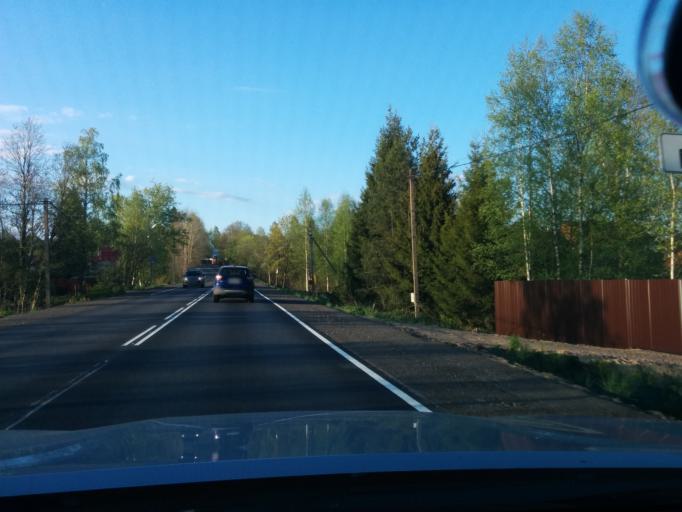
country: RU
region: Leningrad
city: Verkhniye Osel'ki
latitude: 60.2176
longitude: 30.4312
